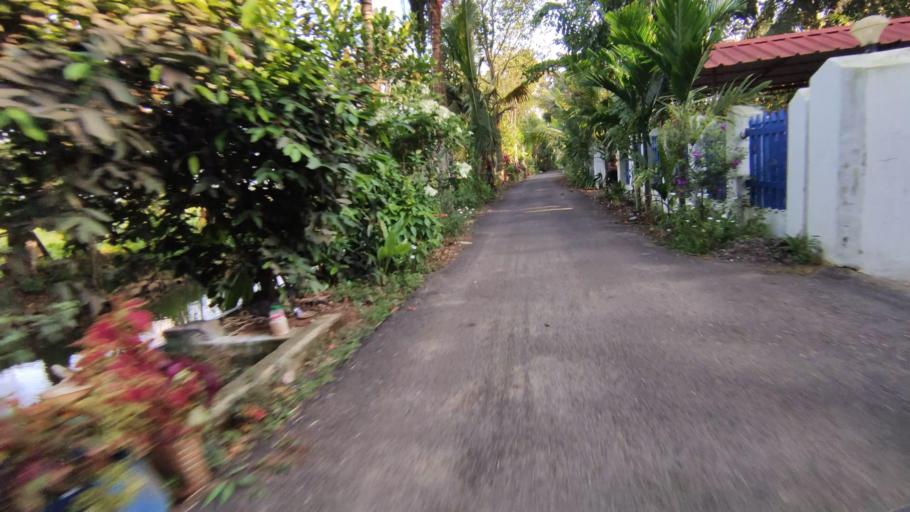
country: IN
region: Kerala
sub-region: Kottayam
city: Kottayam
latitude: 9.5807
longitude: 76.4537
